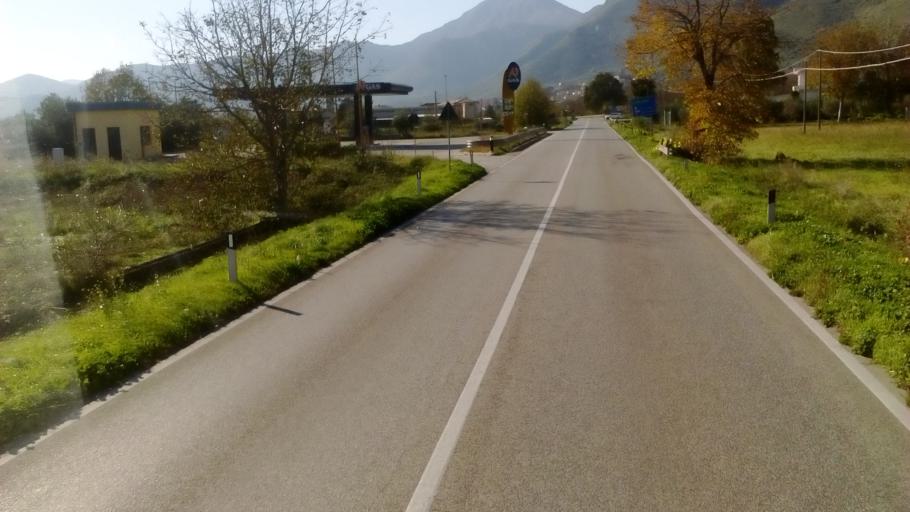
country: IT
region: Molise
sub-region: Provincia di Isernia
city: Pozzilli
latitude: 41.4925
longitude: 14.0650
